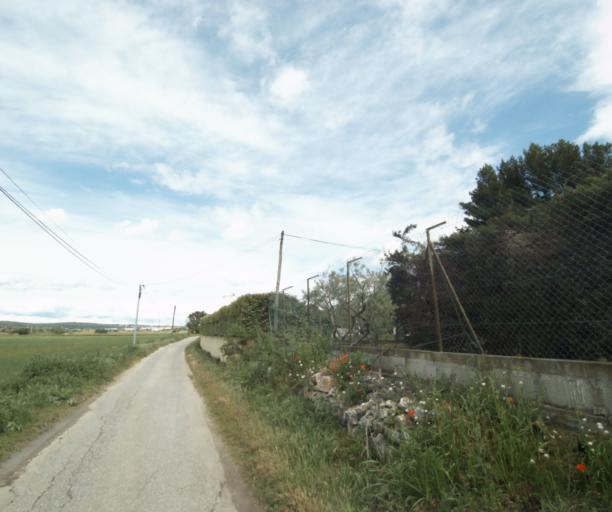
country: FR
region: Provence-Alpes-Cote d'Azur
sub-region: Departement des Bouches-du-Rhone
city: Rognac
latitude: 43.4989
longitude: 5.2300
